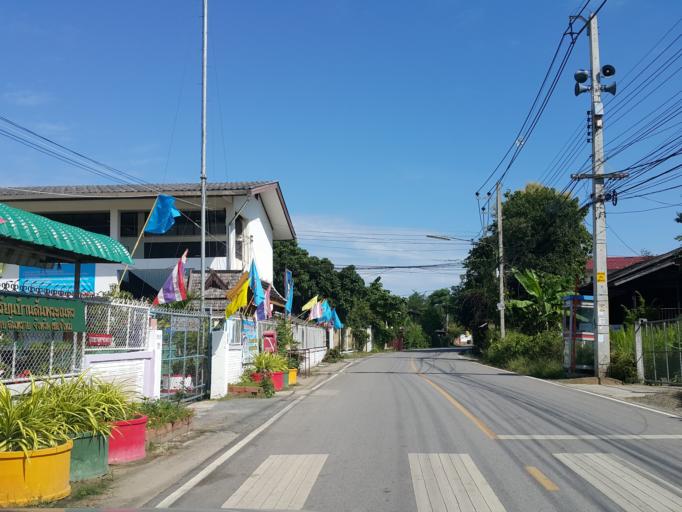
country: TH
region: Chiang Mai
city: San Sai
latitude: 18.8048
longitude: 99.0453
